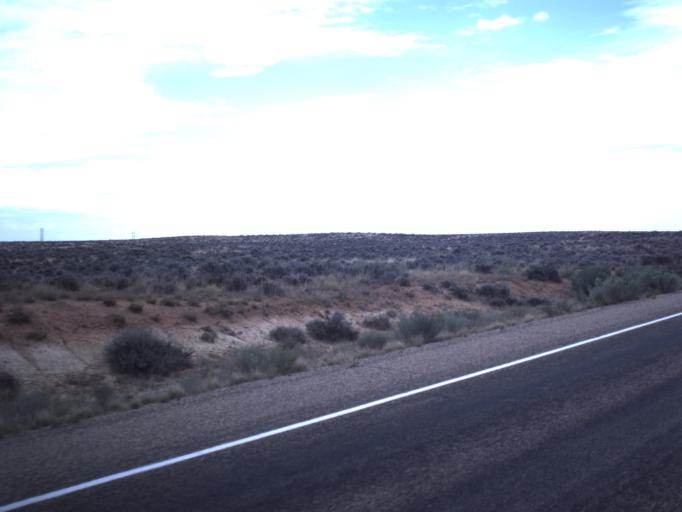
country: US
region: Utah
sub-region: Uintah County
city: Naples
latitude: 40.1573
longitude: -109.3069
